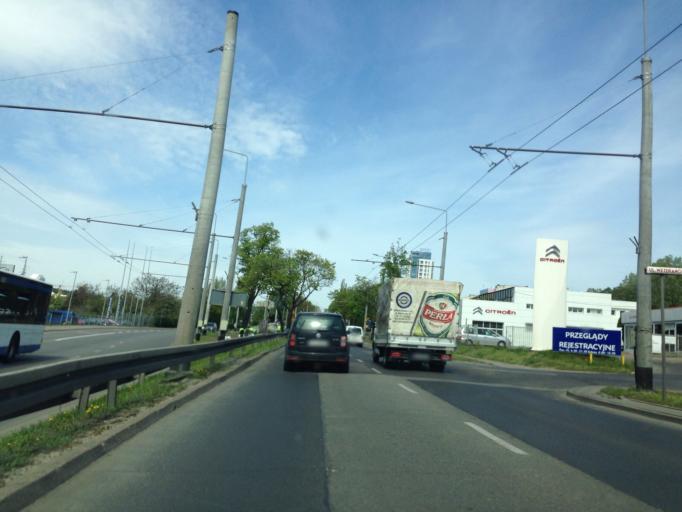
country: PL
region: Pomeranian Voivodeship
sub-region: Gdynia
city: Gdynia
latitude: 54.4864
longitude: 18.5448
